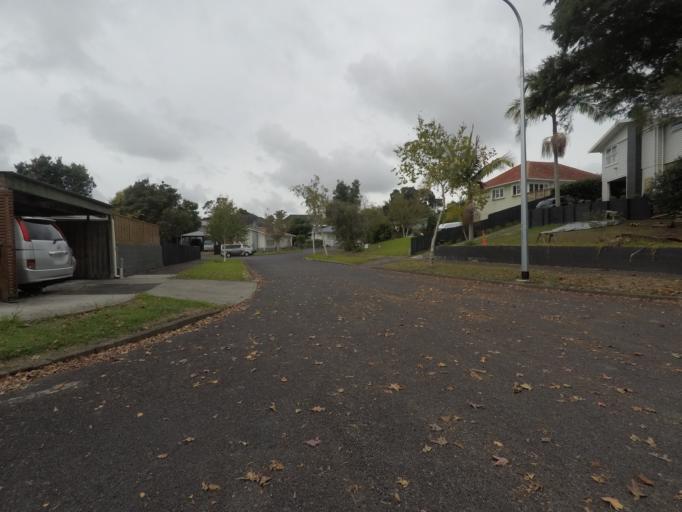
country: NZ
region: Auckland
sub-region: Auckland
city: Rosebank
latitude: -36.8864
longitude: 174.6749
